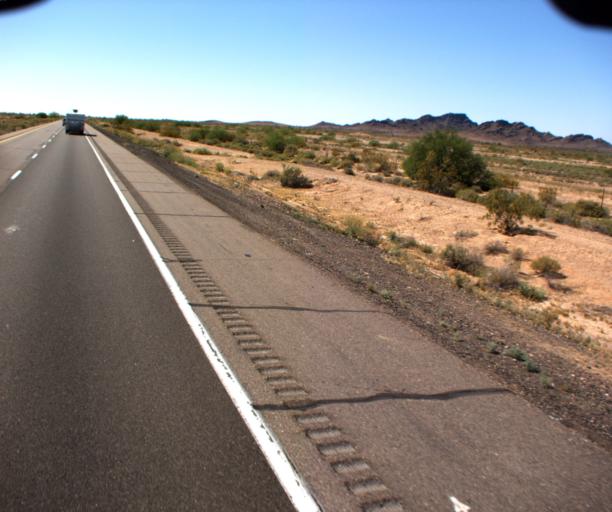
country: US
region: Arizona
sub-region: Maricopa County
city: Gila Bend
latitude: 32.9042
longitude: -112.9946
